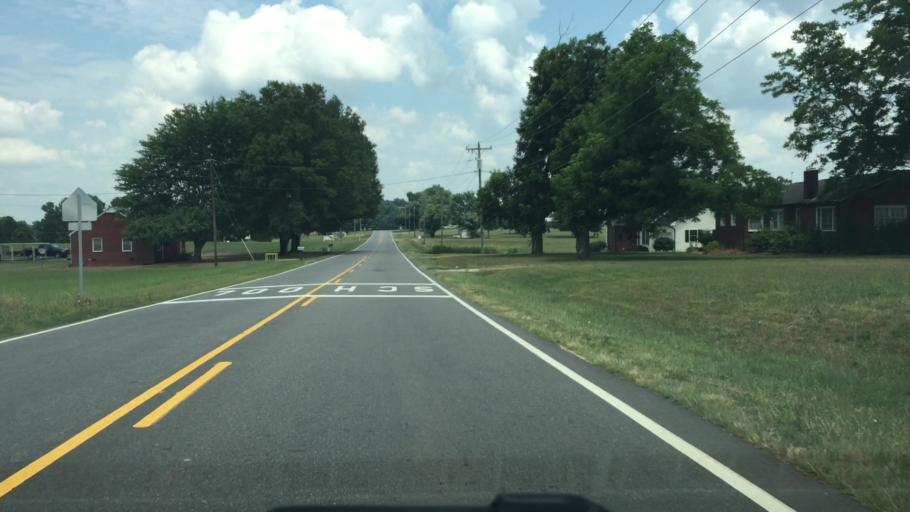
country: US
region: North Carolina
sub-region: Iredell County
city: Troutman
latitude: 35.7179
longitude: -80.8844
